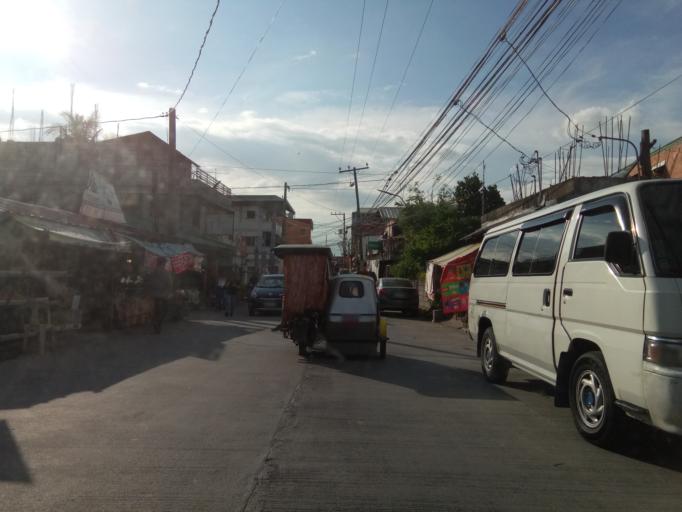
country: PH
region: Calabarzon
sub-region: Province of Cavite
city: Dasmarinas
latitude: 14.2915
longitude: 120.9399
